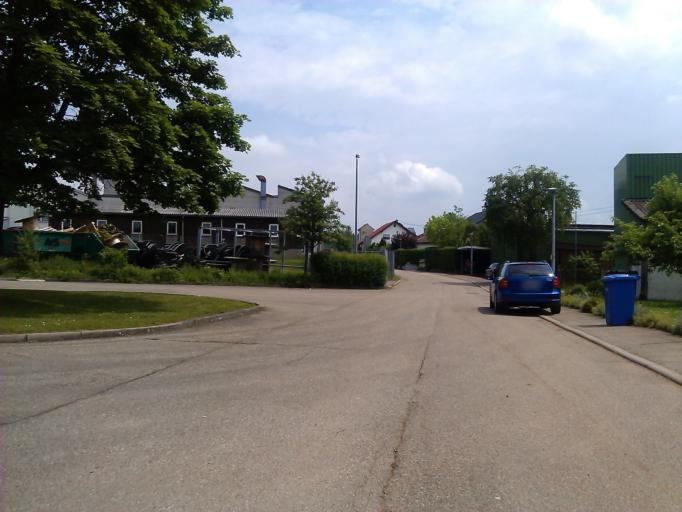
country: DE
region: Baden-Wuerttemberg
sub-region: Regierungsbezirk Stuttgart
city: Zaberfeld
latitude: 49.0624
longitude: 8.9257
